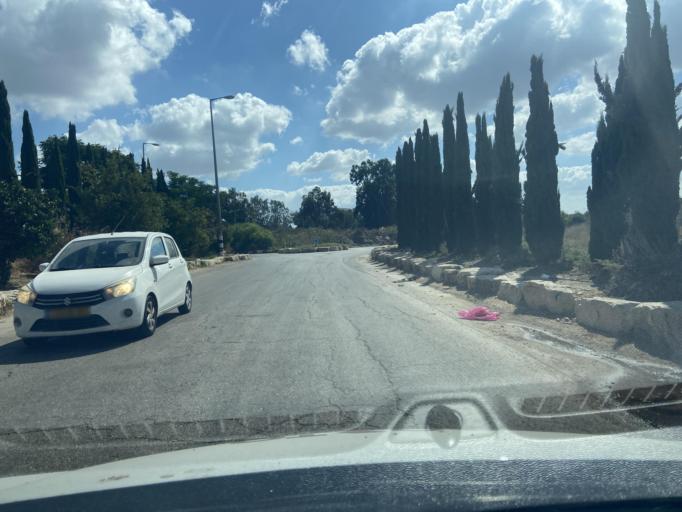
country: IL
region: Central District
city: Yehud
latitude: 32.0251
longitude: 34.8930
